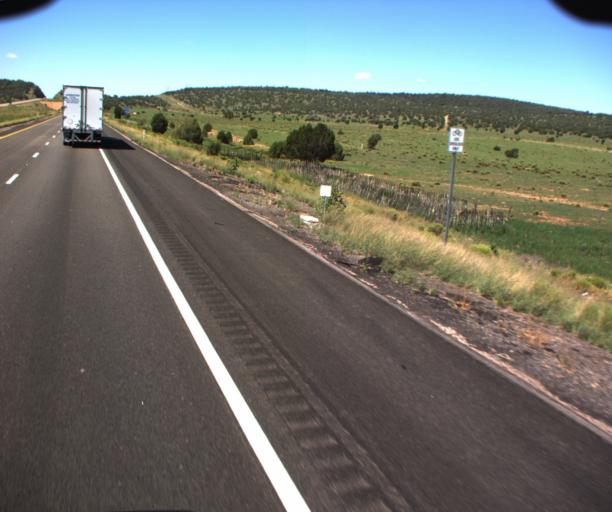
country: US
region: Arizona
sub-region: Mohave County
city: Peach Springs
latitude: 35.2483
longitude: -113.1866
